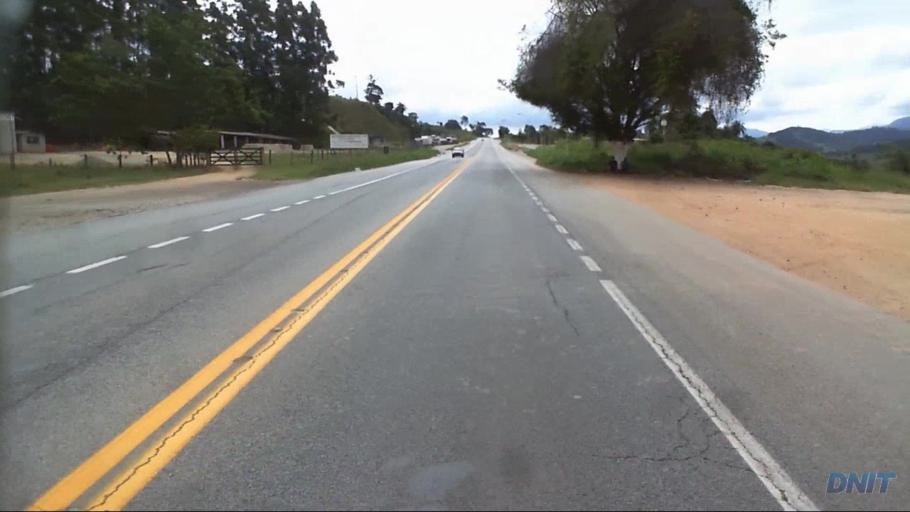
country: BR
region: Minas Gerais
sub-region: Caete
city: Caete
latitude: -19.7403
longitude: -43.5562
